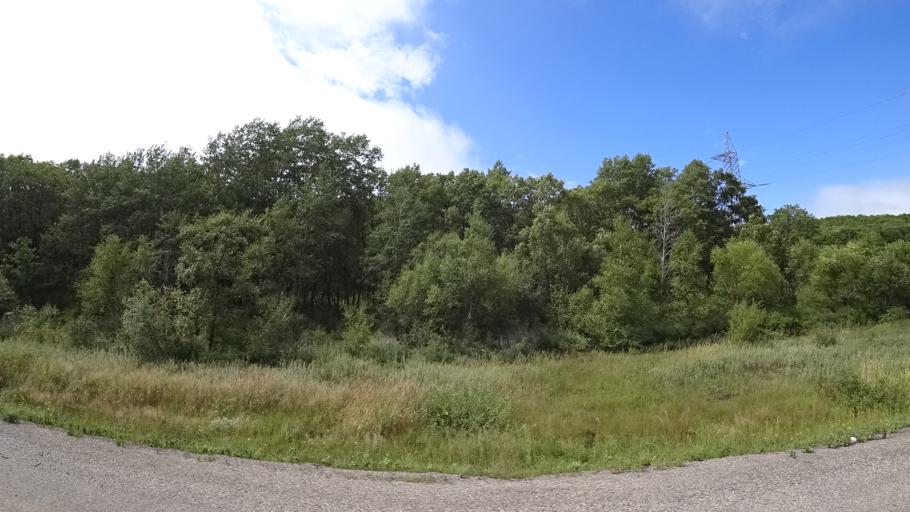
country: RU
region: Primorskiy
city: Lyalichi
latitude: 44.1210
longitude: 132.4202
